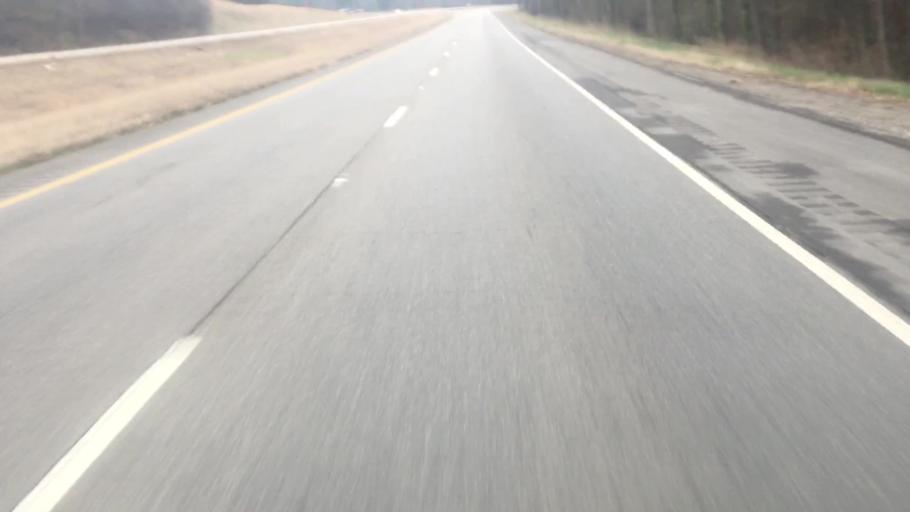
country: US
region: Alabama
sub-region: Walker County
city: Sumiton
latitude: 33.7760
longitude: -87.0785
